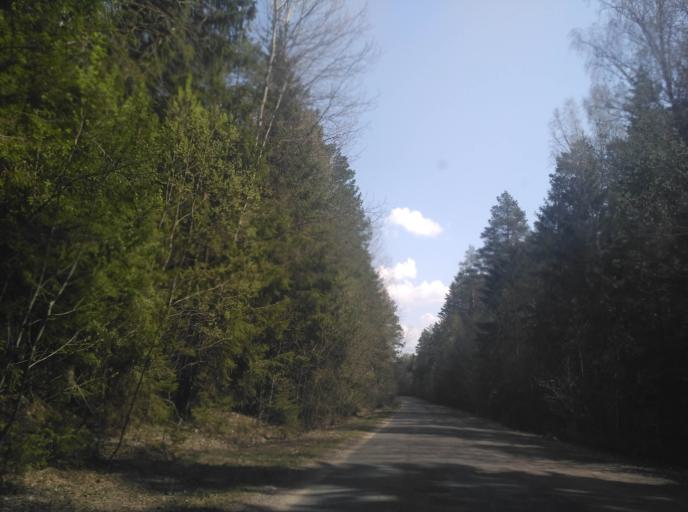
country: BY
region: Minsk
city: Loshnitsa
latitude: 54.4937
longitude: 28.7026
